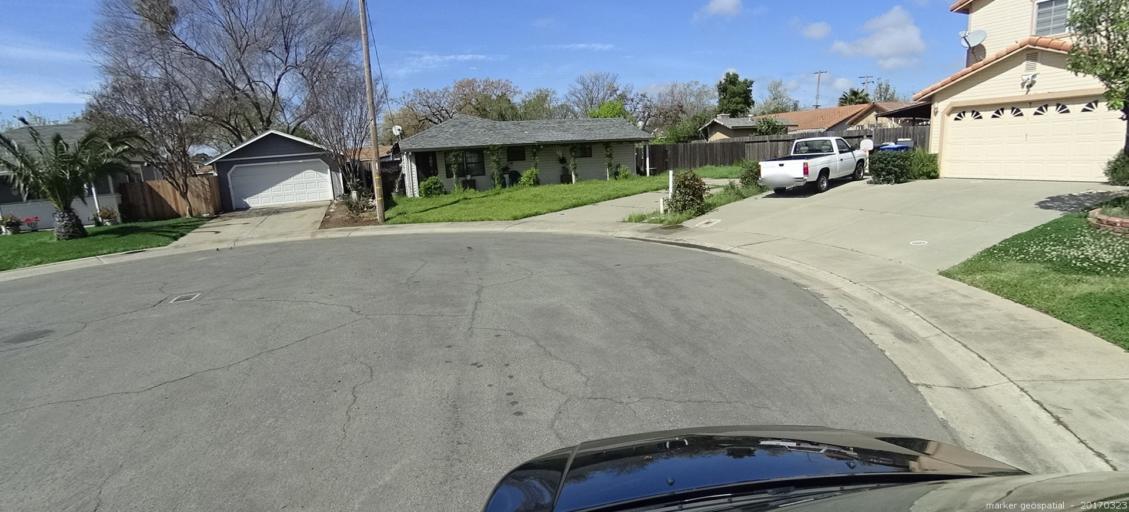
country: US
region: California
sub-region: Sacramento County
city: Florin
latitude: 38.5153
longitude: -121.4246
